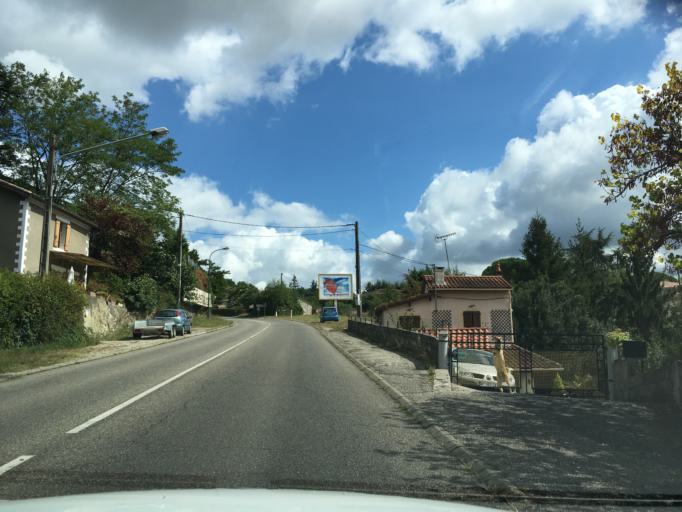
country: FR
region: Aquitaine
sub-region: Departement du Lot-et-Garonne
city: Foulayronnes
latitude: 44.2223
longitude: 0.6321
